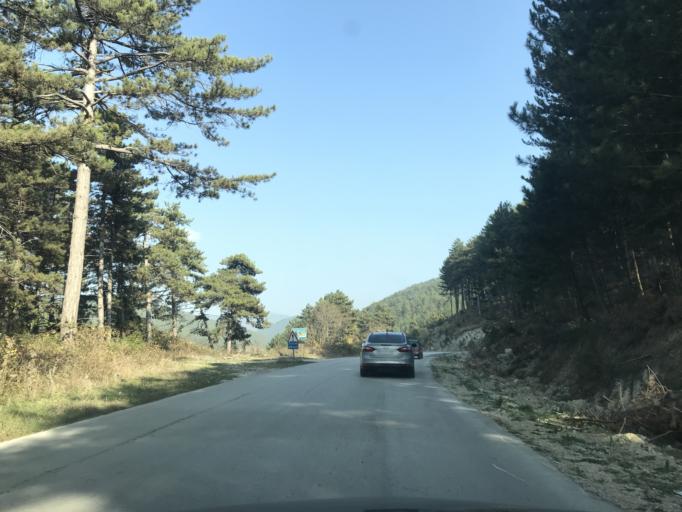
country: TR
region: Bolu
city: Bolu
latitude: 40.7854
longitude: 31.6331
